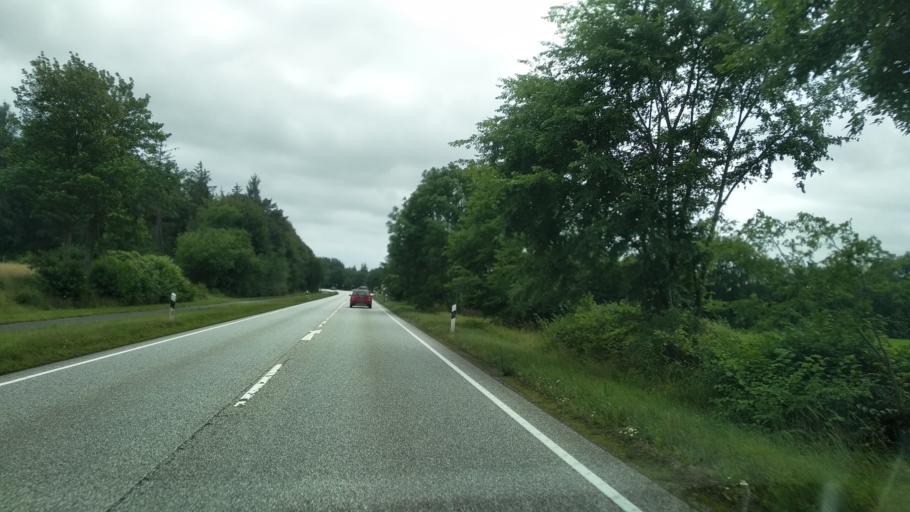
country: DE
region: Schleswig-Holstein
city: Oeversee
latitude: 54.6959
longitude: 9.4332
